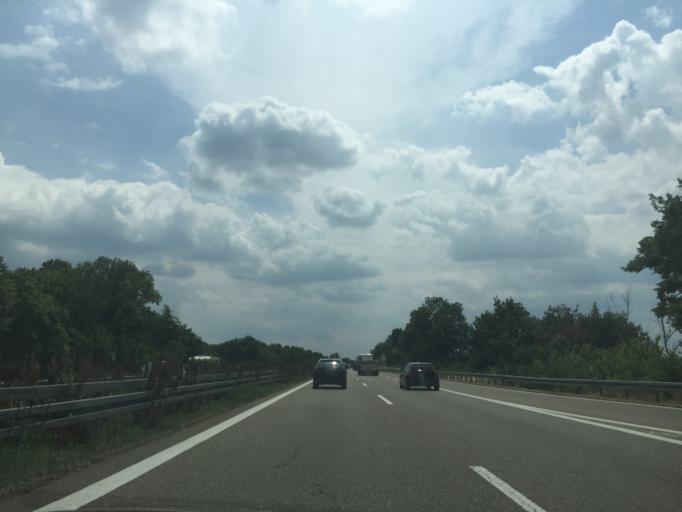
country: DE
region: Baden-Wuerttemberg
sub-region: Karlsruhe Region
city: Schriesheim
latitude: 49.4658
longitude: 8.6443
